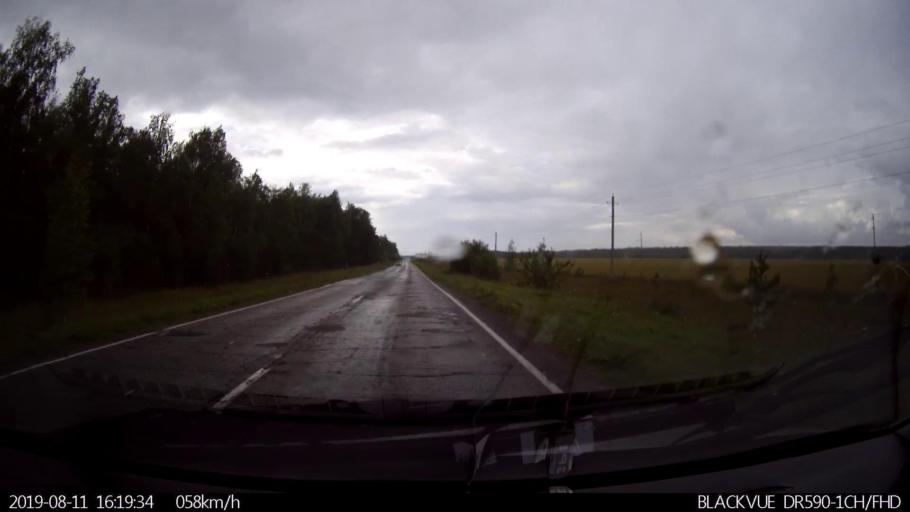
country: RU
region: Ulyanovsk
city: Mayna
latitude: 54.0649
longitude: 47.6067
